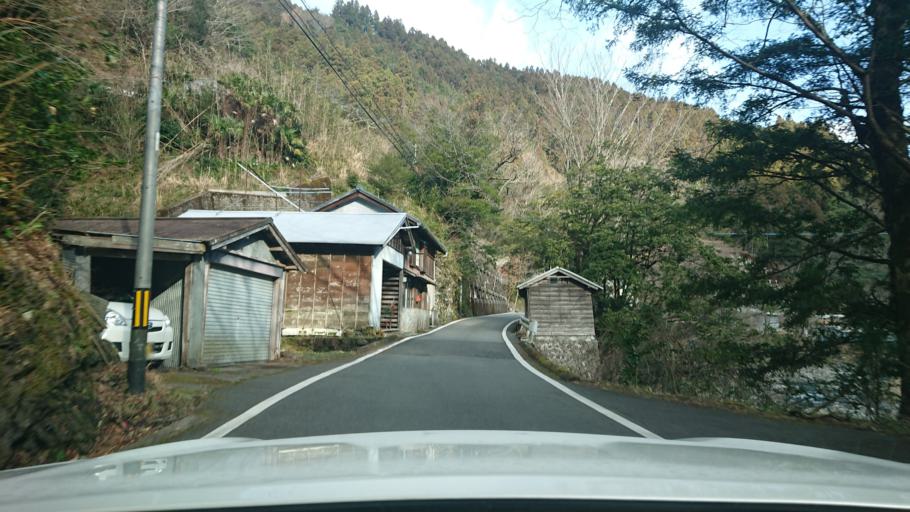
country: JP
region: Tokushima
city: Kamojimacho-jogejima
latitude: 33.9026
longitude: 134.3948
